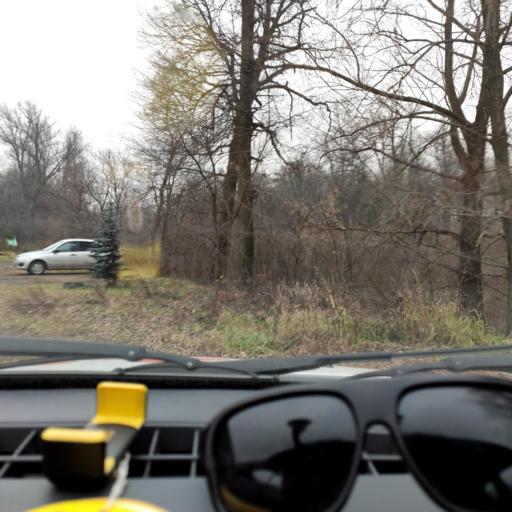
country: RU
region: Bashkortostan
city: Mikhaylovka
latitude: 54.7936
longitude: 55.9380
